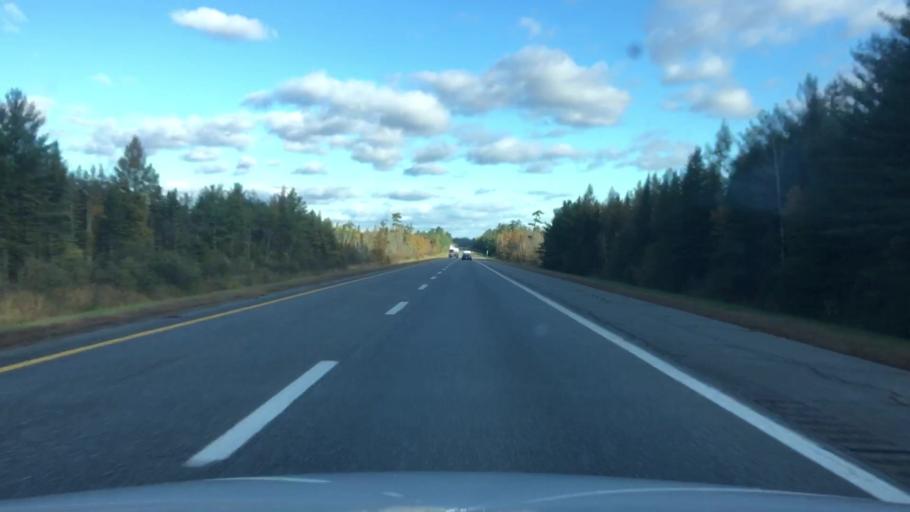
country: US
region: Maine
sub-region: Penobscot County
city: Greenbush
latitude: 45.1283
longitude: -68.6960
